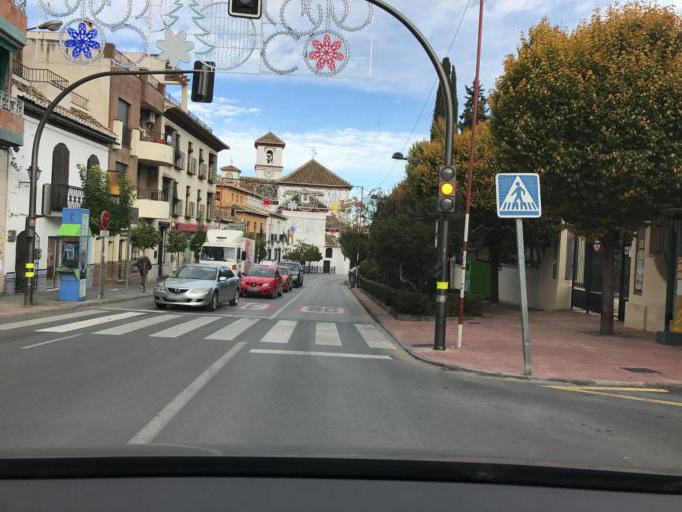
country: ES
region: Andalusia
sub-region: Provincia de Granada
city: Zubia
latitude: 37.1199
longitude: -3.5843
